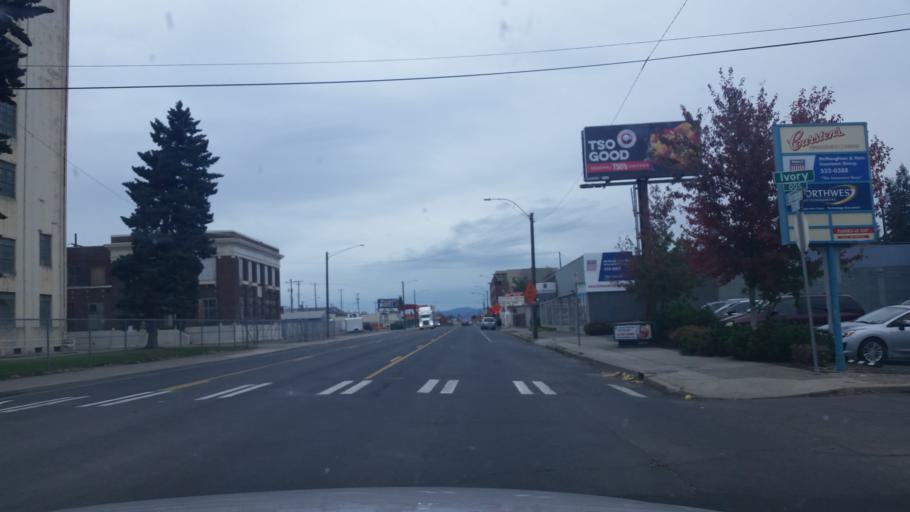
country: US
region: Washington
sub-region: Spokane County
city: Spokane
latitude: 47.6571
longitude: -117.3927
